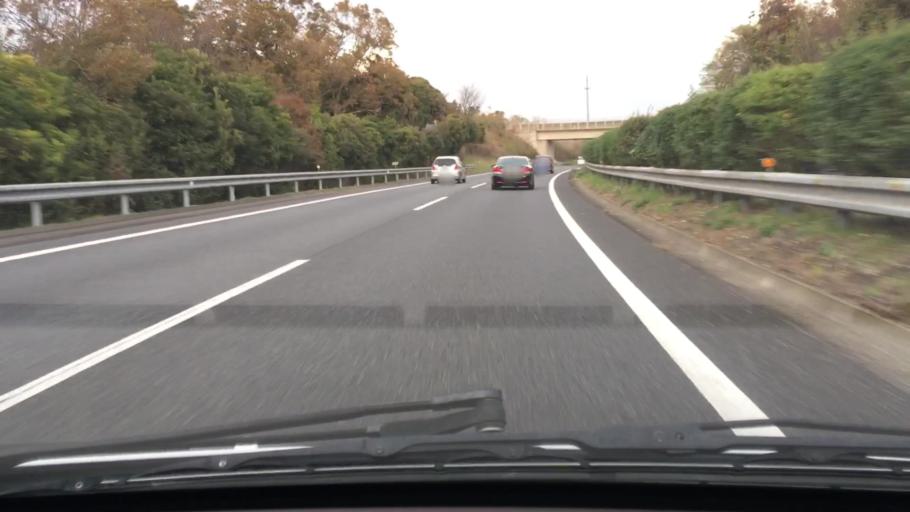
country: JP
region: Chiba
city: Kisarazu
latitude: 35.4226
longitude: 140.0158
